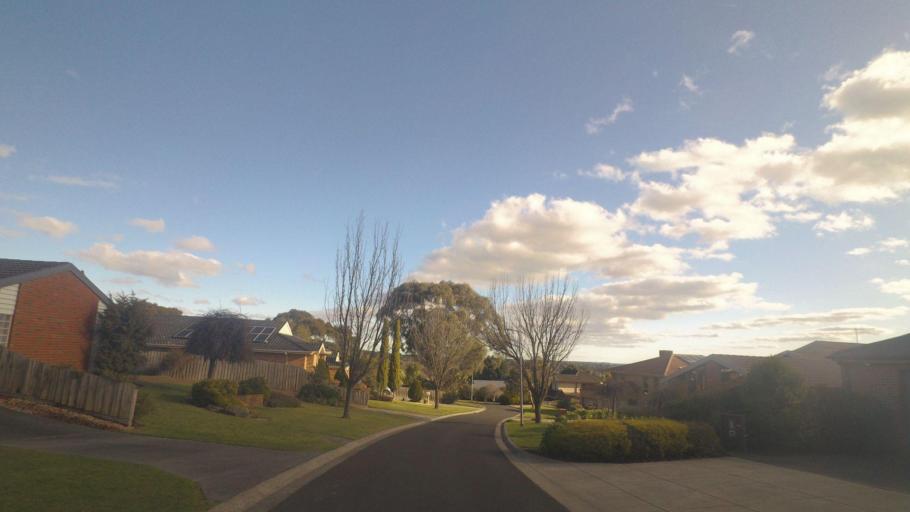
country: AU
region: Victoria
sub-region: Knox
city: Ferntree Gully
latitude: -37.9099
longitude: 145.2849
